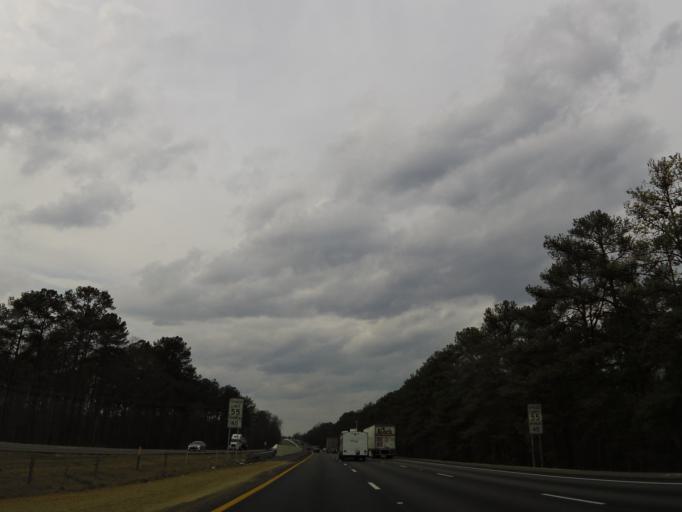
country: US
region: South Carolina
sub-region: Lexington County
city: Pineridge
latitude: 33.9105
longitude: -81.0555
